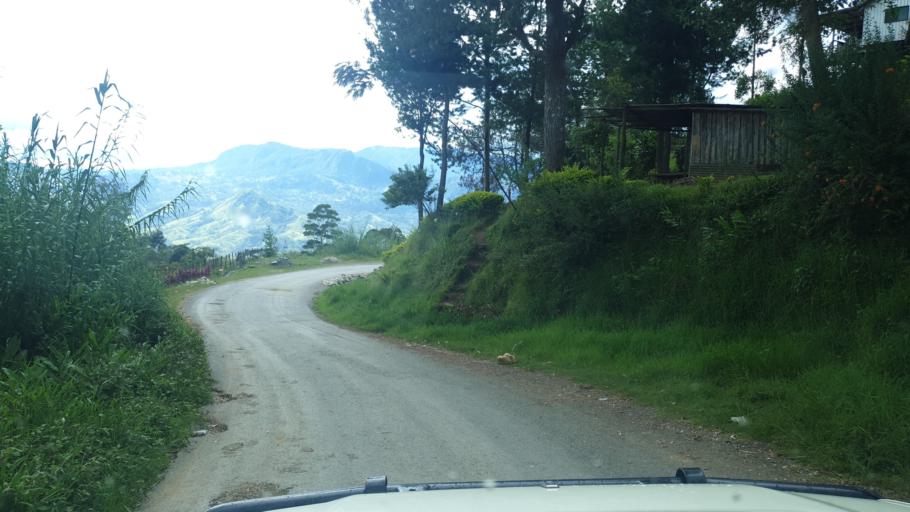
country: PG
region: Chimbu
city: Kundiawa
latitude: -6.1654
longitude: 145.1340
